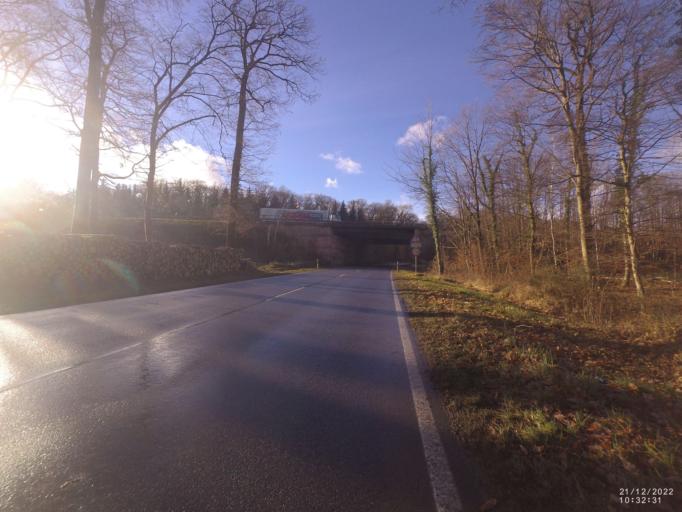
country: DE
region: Rheinland-Pfalz
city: Waldorf
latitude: 50.5100
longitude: 7.2156
